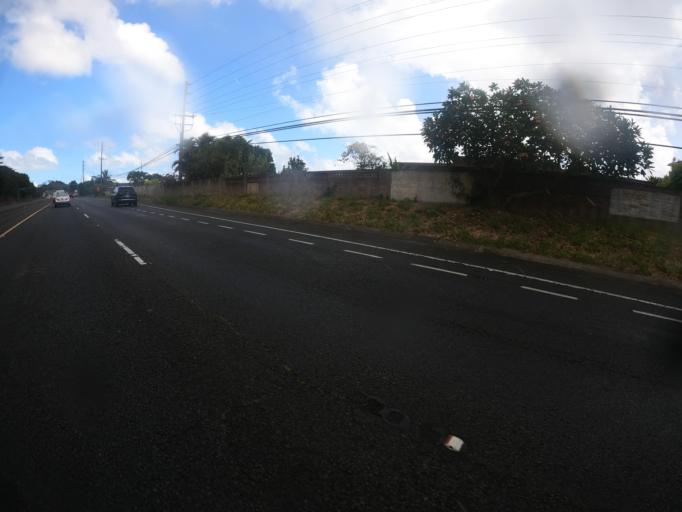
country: US
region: Hawaii
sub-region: Honolulu County
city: Waimanalo
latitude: 21.3669
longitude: -157.7392
